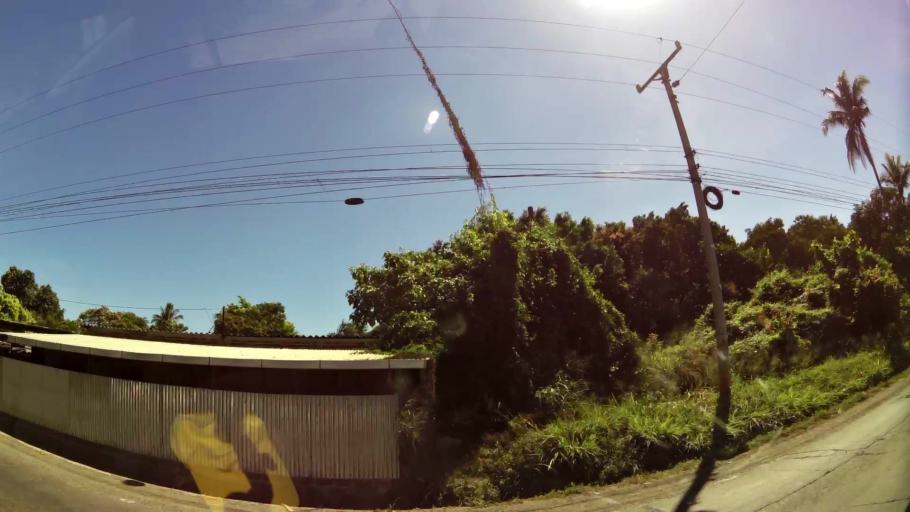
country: SV
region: La Libertad
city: San Juan Opico
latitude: 13.7863
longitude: -89.3709
